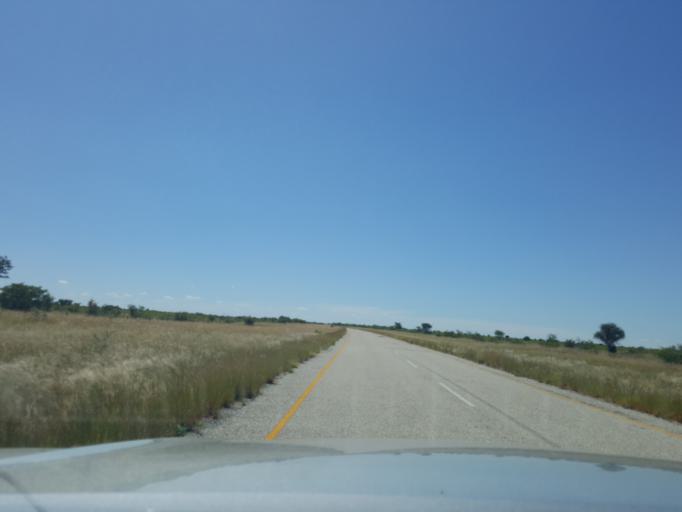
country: BW
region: Central
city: Gweta
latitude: -20.2306
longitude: 24.9748
